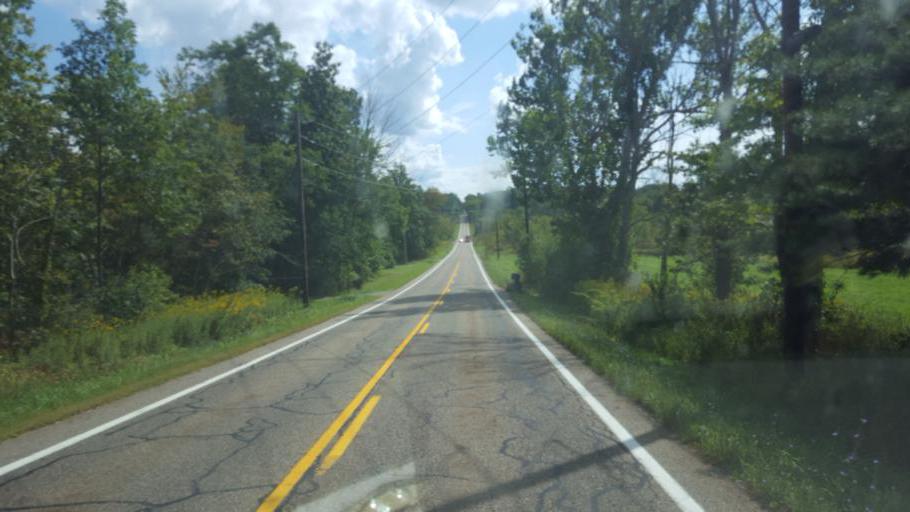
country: US
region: Ohio
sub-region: Portage County
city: Hiram
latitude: 41.2848
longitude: -81.1445
